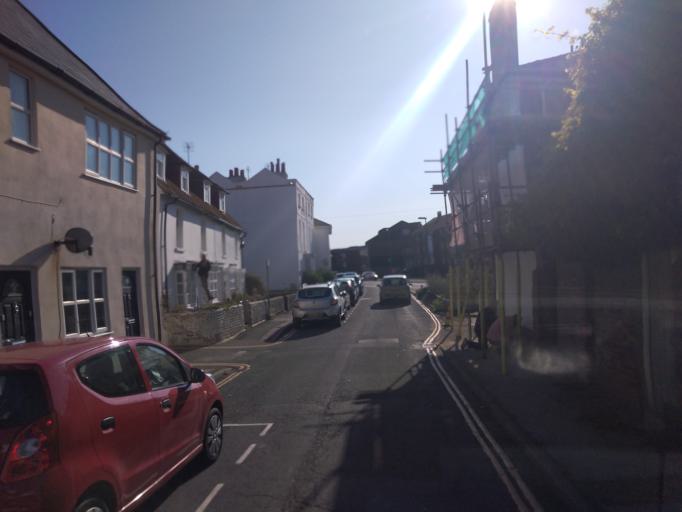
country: GB
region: England
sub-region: East Sussex
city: Seaford
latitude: 50.7706
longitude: 0.1019
